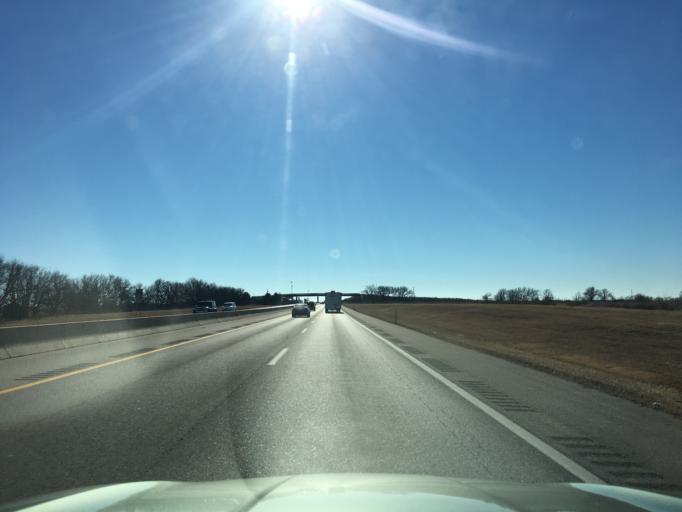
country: US
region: Oklahoma
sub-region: Kay County
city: Blackwell
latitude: 37.0320
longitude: -97.3383
